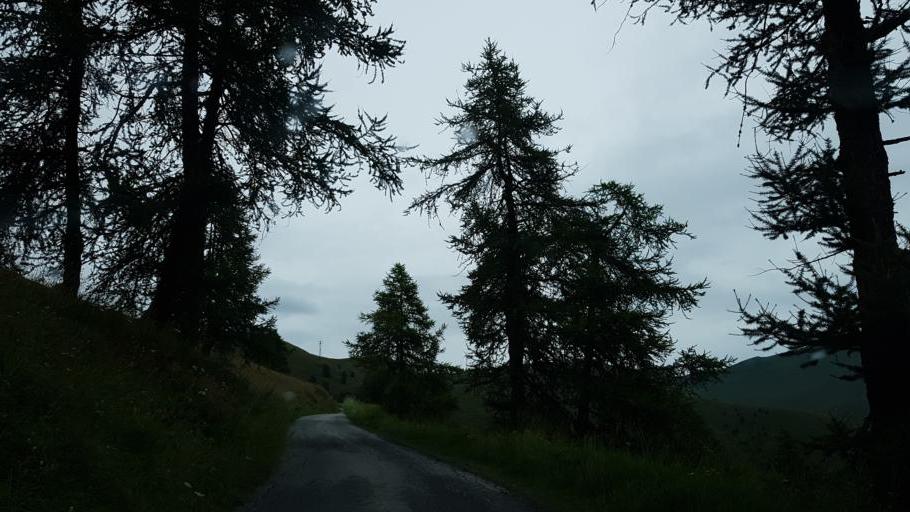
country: IT
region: Piedmont
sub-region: Provincia di Cuneo
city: Stroppo
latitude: 44.5187
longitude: 7.1051
